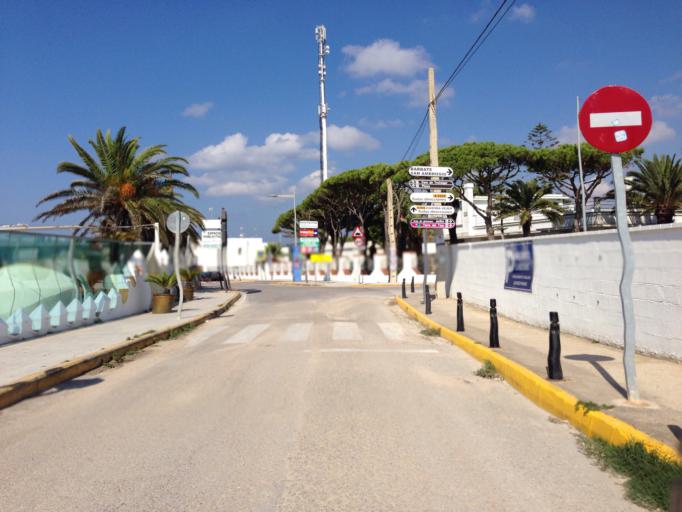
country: ES
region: Andalusia
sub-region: Provincia de Cadiz
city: Vejer de la Frontera
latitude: 36.1852
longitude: -6.0088
